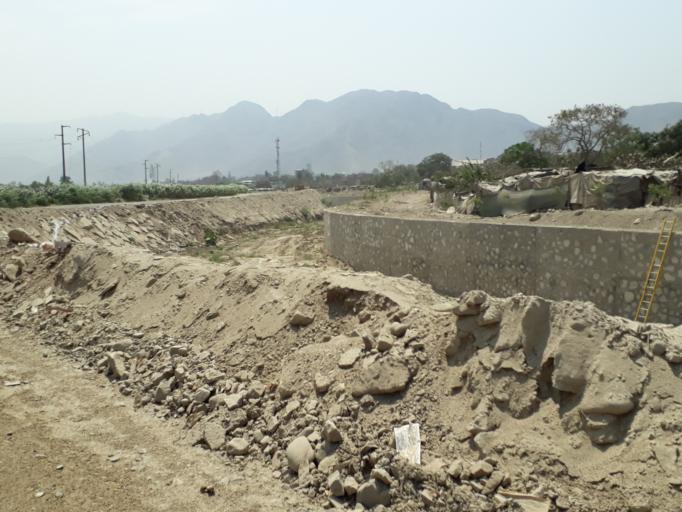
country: PE
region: Lima
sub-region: Lima
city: Santa Maria
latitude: -11.9959
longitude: -76.9130
